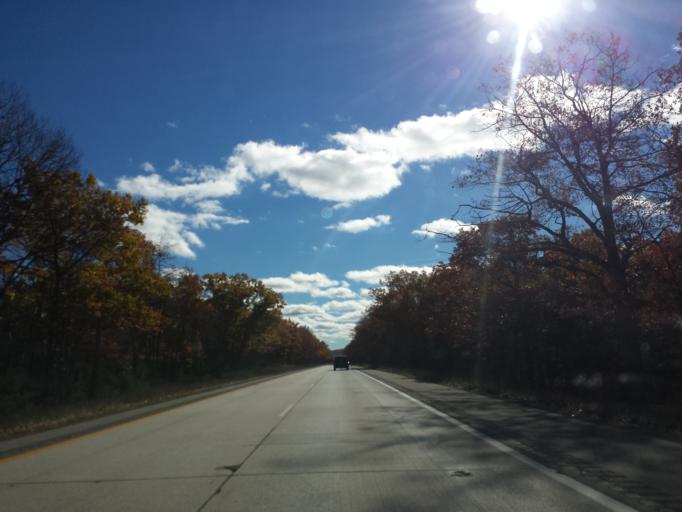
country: US
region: Michigan
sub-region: Cheboygan County
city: Indian River
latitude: 45.4756
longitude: -84.6159
